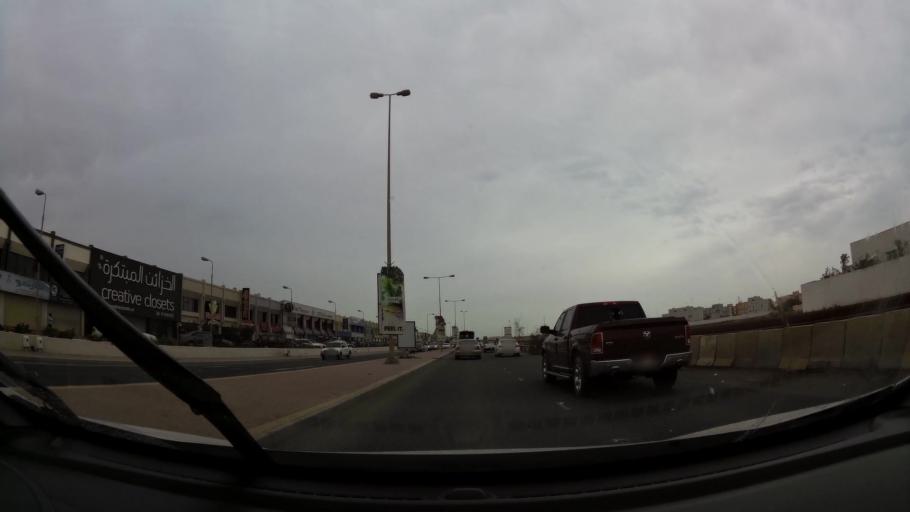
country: BH
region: Central Governorate
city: Madinat Hamad
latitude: 26.1661
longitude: 50.4689
